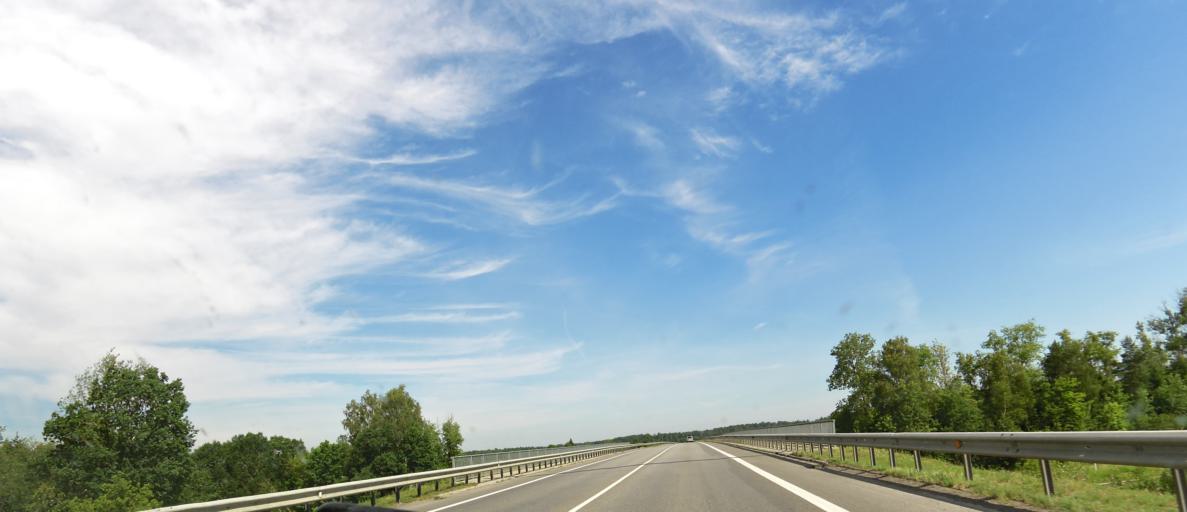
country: LT
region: Panevezys
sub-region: Panevezys City
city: Panevezys
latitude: 55.7450
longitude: 24.2772
